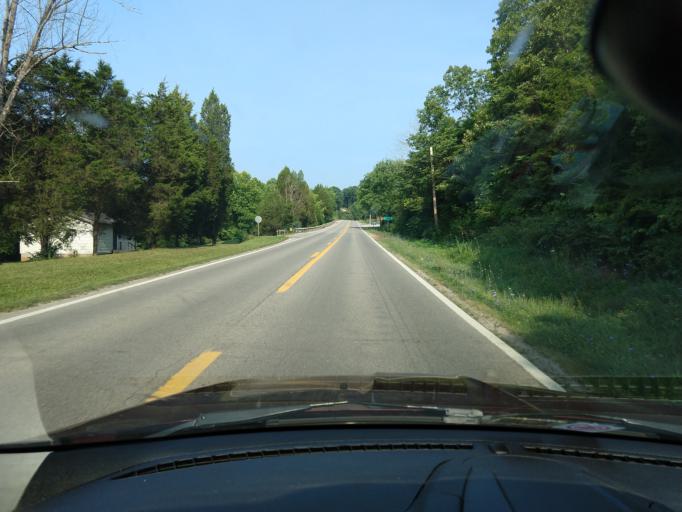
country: US
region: West Virginia
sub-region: Jackson County
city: Ripley
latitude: 38.8399
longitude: -81.7898
